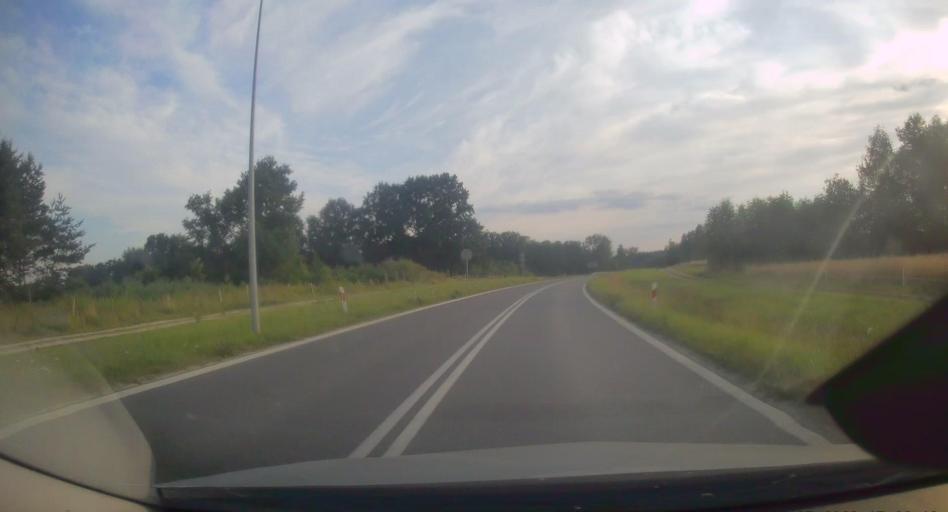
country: PL
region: Lesser Poland Voivodeship
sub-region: Powiat brzeski
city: Przyborow
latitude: 50.0230
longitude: 20.6289
